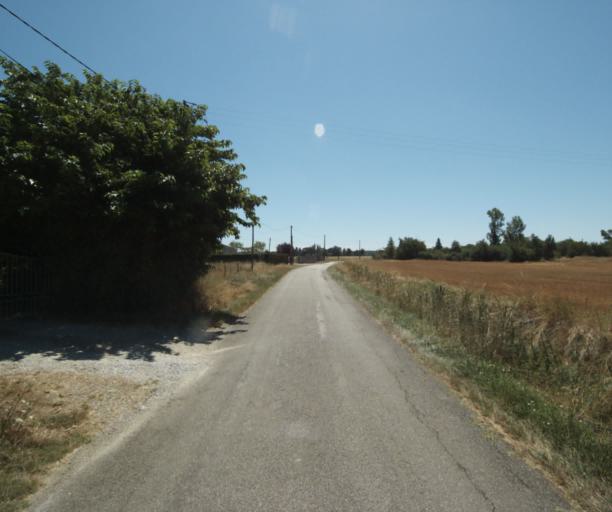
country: FR
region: Midi-Pyrenees
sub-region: Departement de la Haute-Garonne
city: Saint-Felix-Lauragais
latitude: 43.4494
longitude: 1.9375
